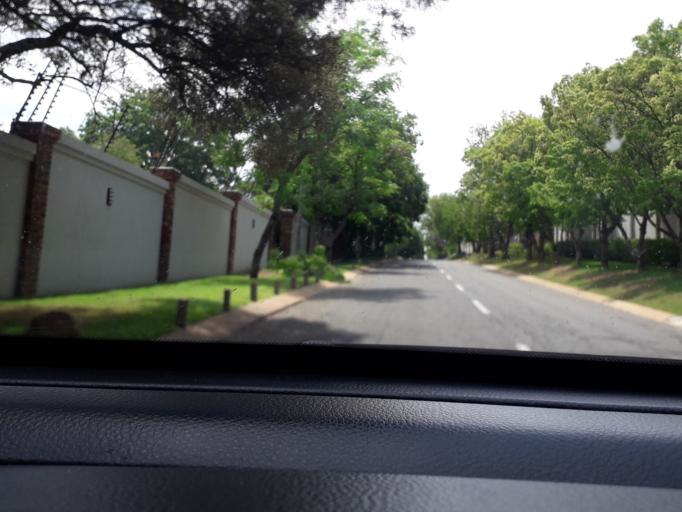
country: ZA
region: Gauteng
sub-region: City of Johannesburg Metropolitan Municipality
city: Midrand
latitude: -26.0670
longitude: 28.0428
